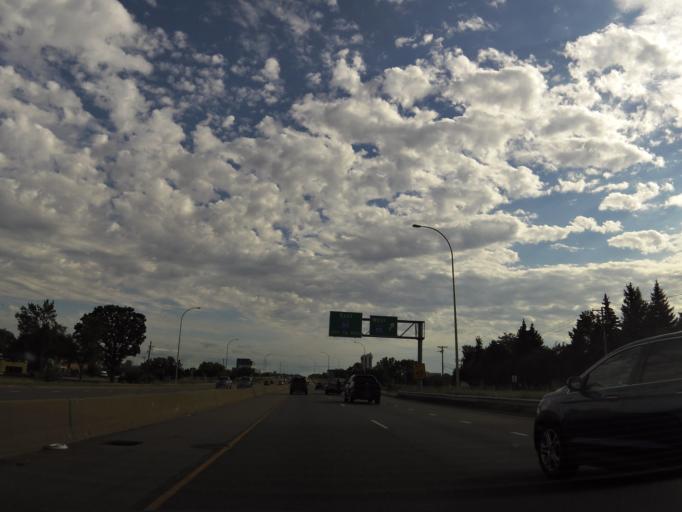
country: US
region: Minnesota
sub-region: Hennepin County
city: New Hope
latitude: 44.9871
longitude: -93.4008
